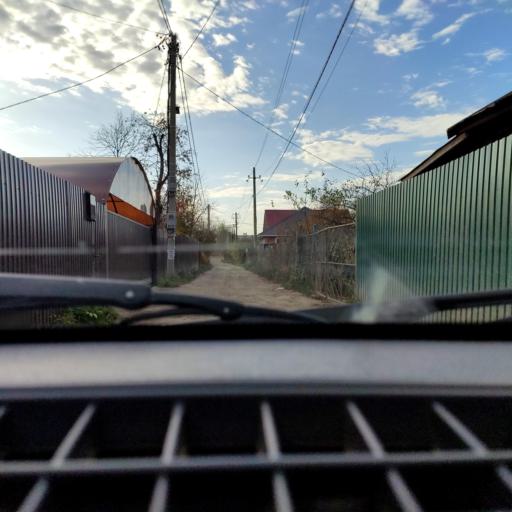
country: RU
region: Bashkortostan
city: Avdon
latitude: 54.7137
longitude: 55.8149
